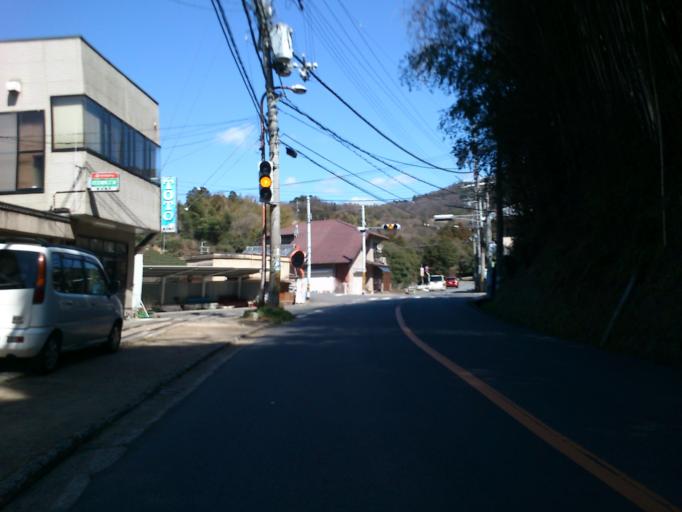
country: JP
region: Nara
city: Nara-shi
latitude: 34.7805
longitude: 135.8809
